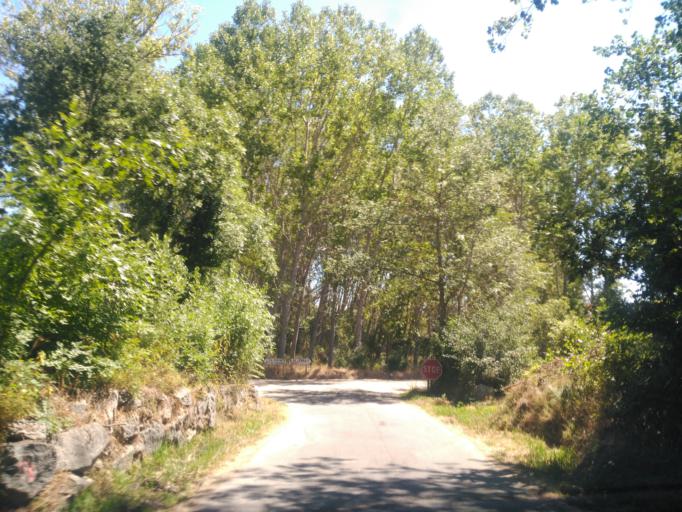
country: ES
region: Castille and Leon
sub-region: Provincia de Zamora
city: Cobreros
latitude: 42.0893
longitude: -6.7140
